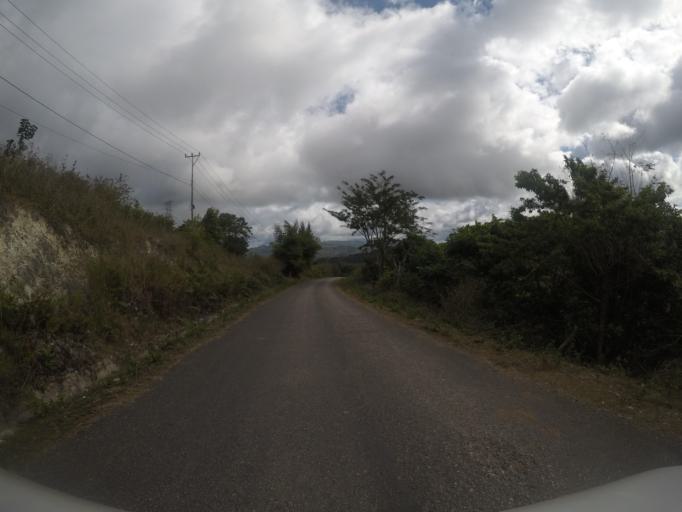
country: TL
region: Lautem
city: Lospalos
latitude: -8.5355
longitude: 126.9131
